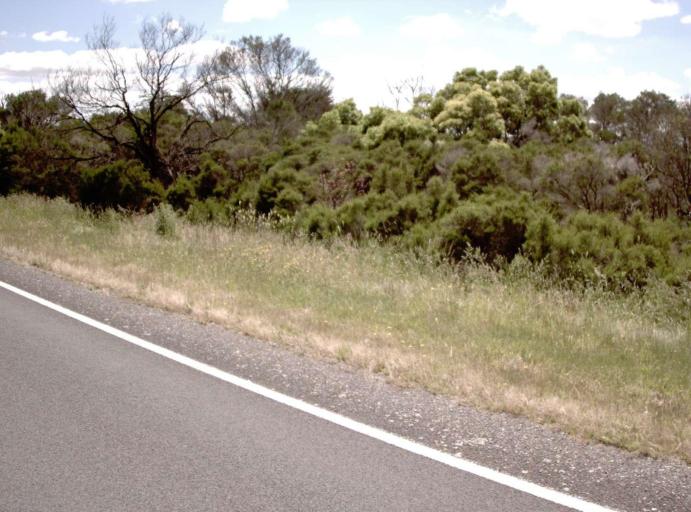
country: AU
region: Victoria
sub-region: Cardinia
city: Koo-Wee-Rup
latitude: -38.2988
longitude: 145.5436
